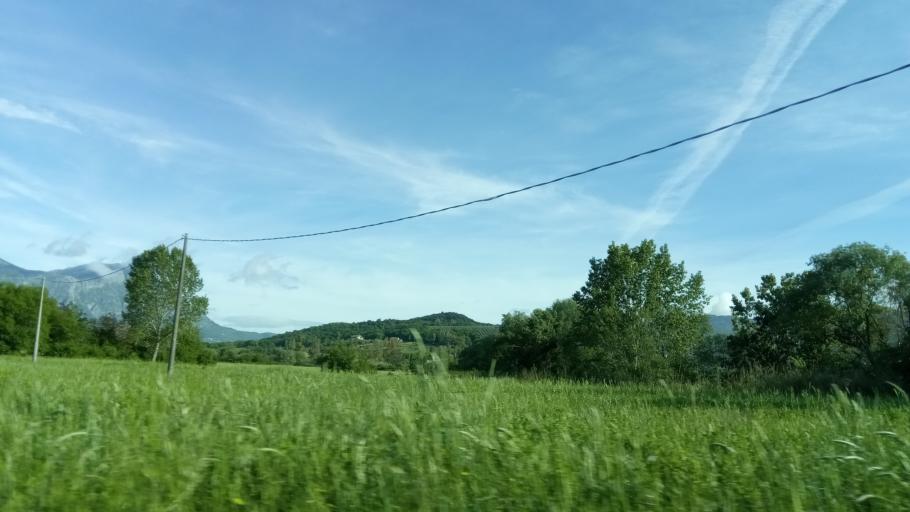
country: IT
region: Latium
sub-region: Provincia di Latina
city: Grunuovo-Campomaggiore San Luca
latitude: 41.2851
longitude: 13.7746
